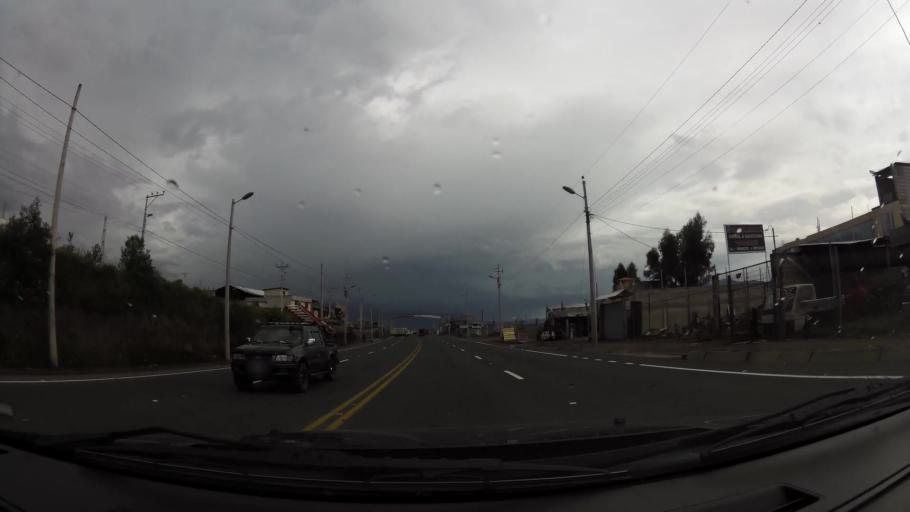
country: EC
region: Pichincha
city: Sangolqui
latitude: -0.3766
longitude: -78.5525
